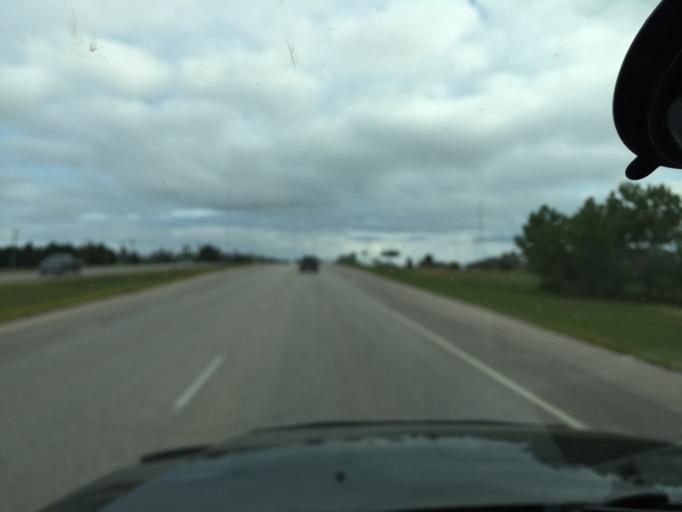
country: US
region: South Dakota
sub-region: Pennington County
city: Rapid City
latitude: 44.0371
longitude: -103.2465
